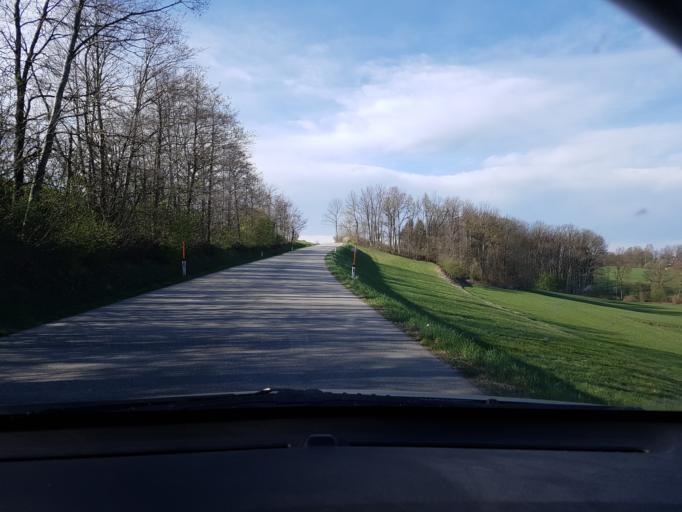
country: AT
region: Upper Austria
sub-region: Politischer Bezirk Linz-Land
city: Sankt Florian
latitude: 48.1512
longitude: 14.3848
